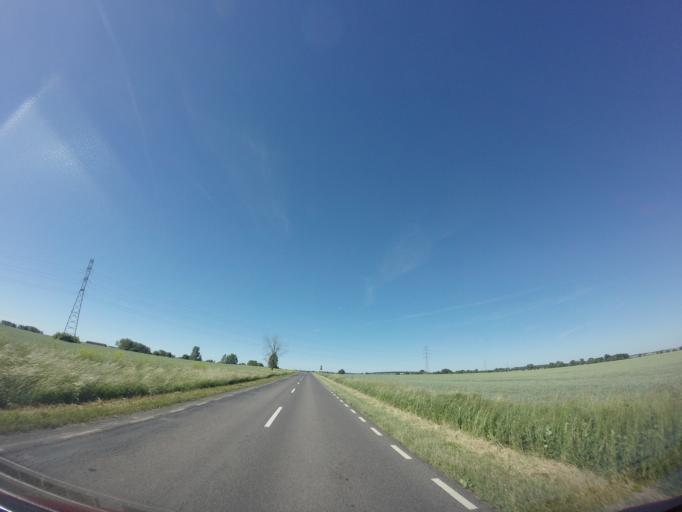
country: PL
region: West Pomeranian Voivodeship
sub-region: Powiat pyrzycki
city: Przelewice
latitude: 53.1461
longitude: 15.0236
